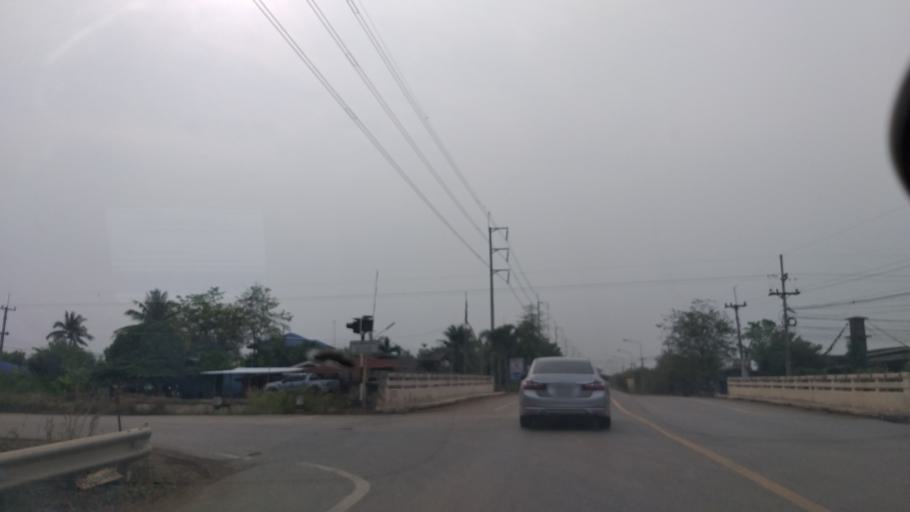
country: TH
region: Chachoengsao
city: Plaeng Yao
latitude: 13.5845
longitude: 101.2203
